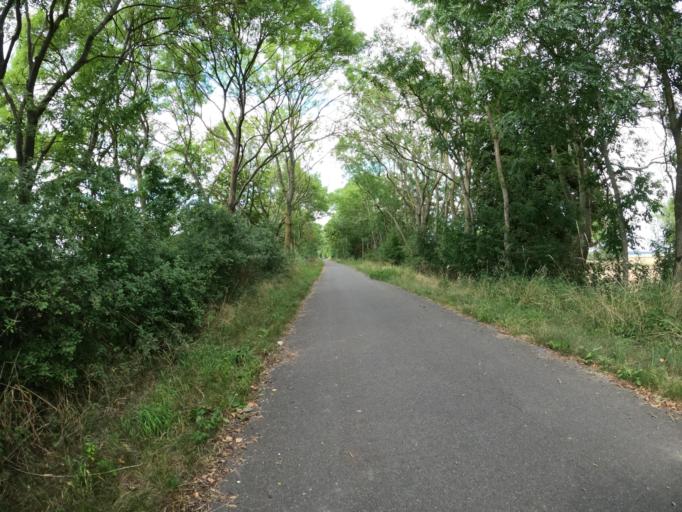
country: DE
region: Mecklenburg-Vorpommern
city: Woldegk
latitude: 53.3803
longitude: 13.5887
